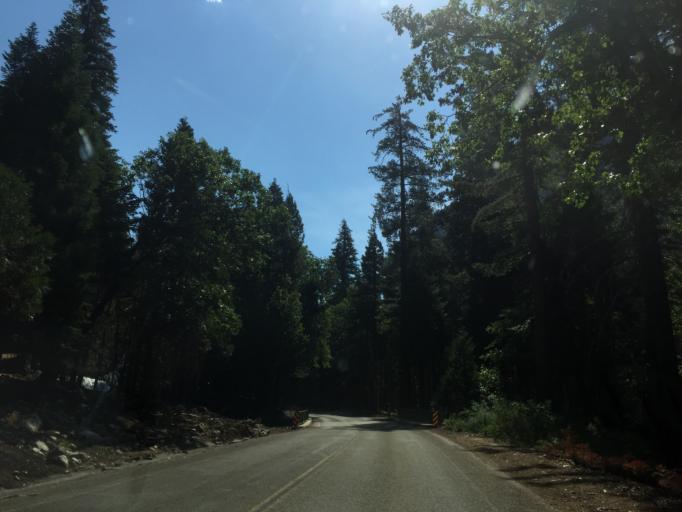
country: US
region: California
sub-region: Tulare County
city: Three Rivers
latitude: 36.7912
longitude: -118.6038
